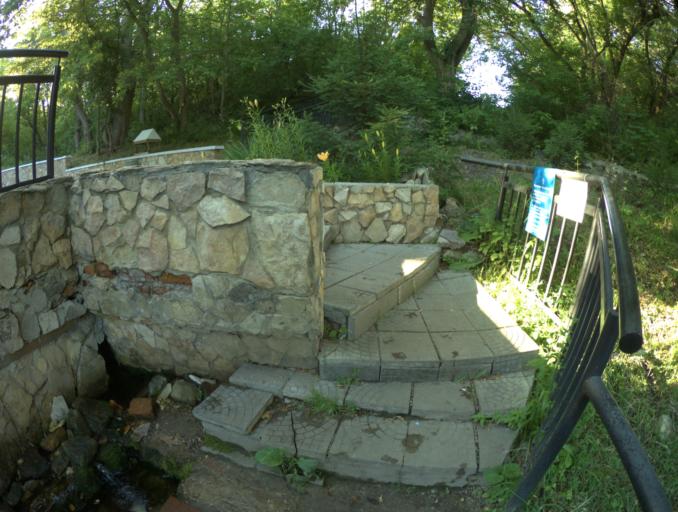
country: RU
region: Saratov
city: Yelshanka
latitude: 51.8146
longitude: 46.4333
